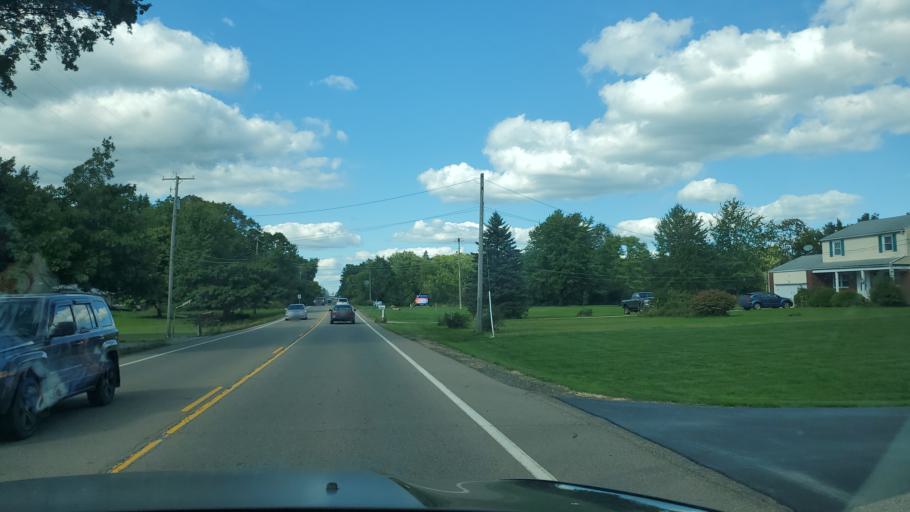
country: US
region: Ohio
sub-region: Mahoning County
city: Austintown
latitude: 41.0769
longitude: -80.7625
